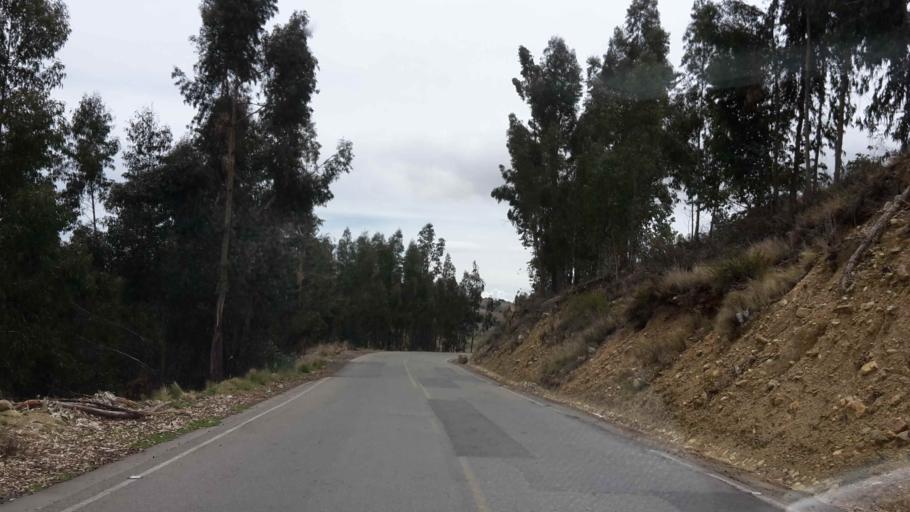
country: BO
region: Cochabamba
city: Arani
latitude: -17.4779
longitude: -65.6244
